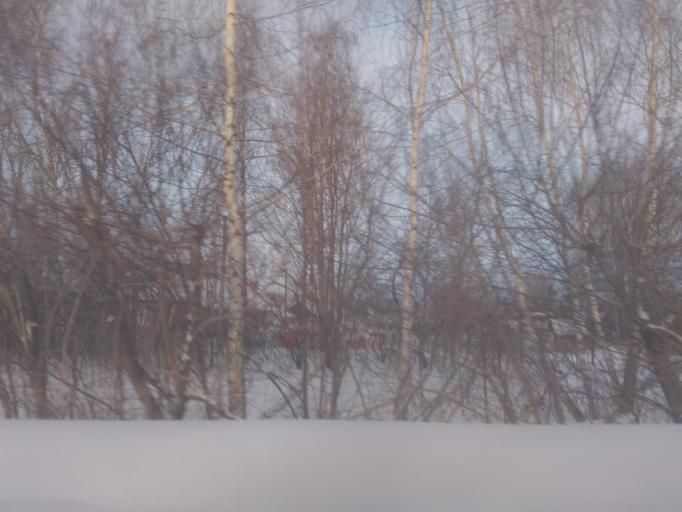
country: RU
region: Ulyanovsk
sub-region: Ulyanovskiy Rayon
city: Ulyanovsk
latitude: 54.3612
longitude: 48.3487
